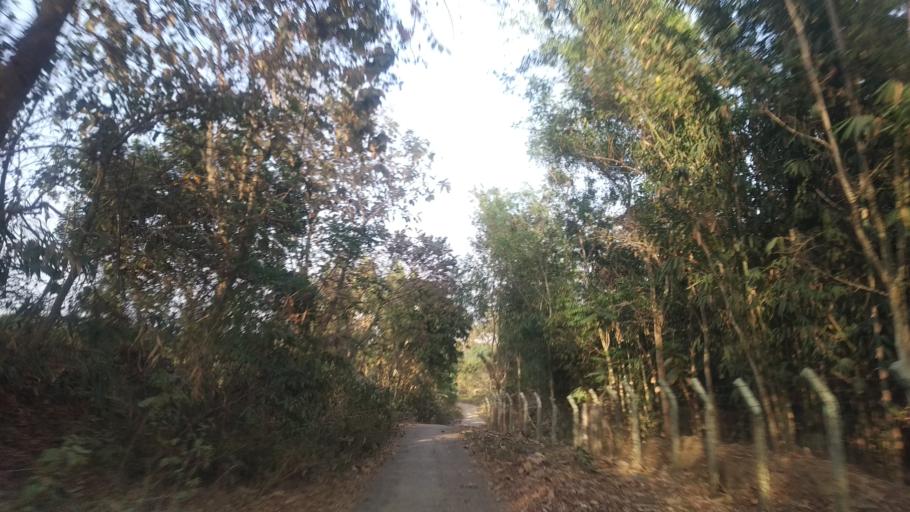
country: IN
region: Tripura
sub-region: West Tripura
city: Sonamura
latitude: 23.4354
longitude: 91.3578
